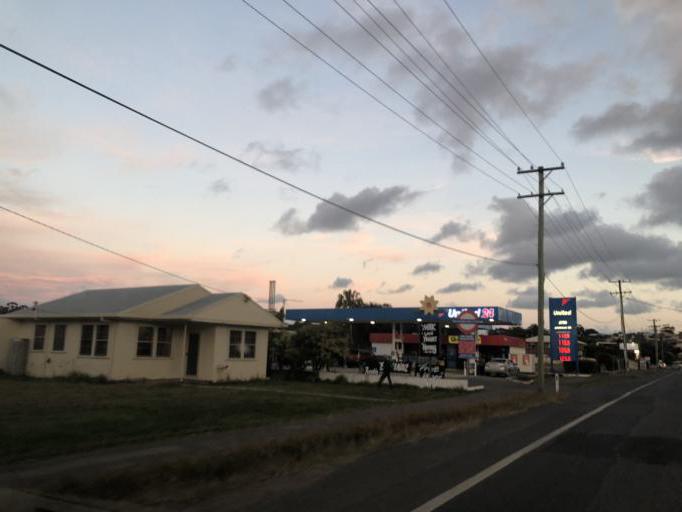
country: AU
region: New South Wales
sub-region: Coffs Harbour
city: Woolgoolga
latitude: -30.1101
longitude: 153.1901
